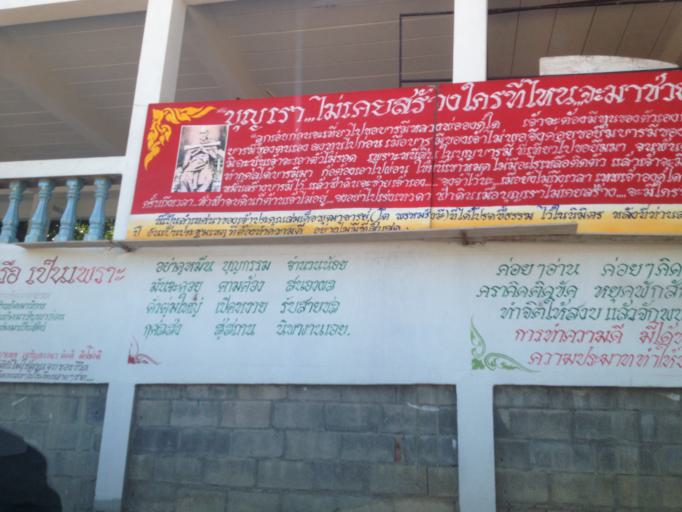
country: TH
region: Chiang Mai
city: Chom Thong
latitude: 18.3850
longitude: 98.6765
